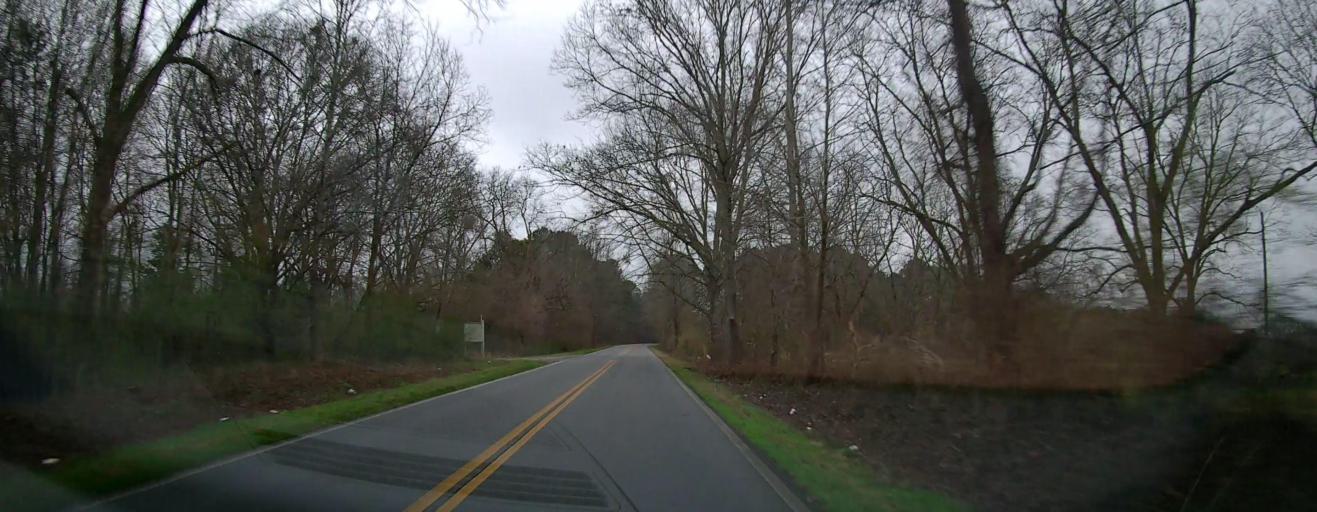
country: US
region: Georgia
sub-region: Spalding County
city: East Griffin
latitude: 33.1638
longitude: -84.2059
